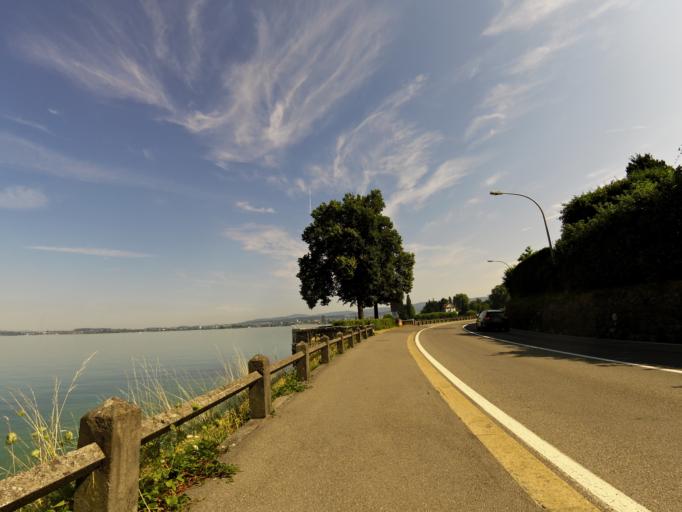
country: CH
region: Zug
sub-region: Zug
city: Zug
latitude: 47.1518
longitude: 8.5088
